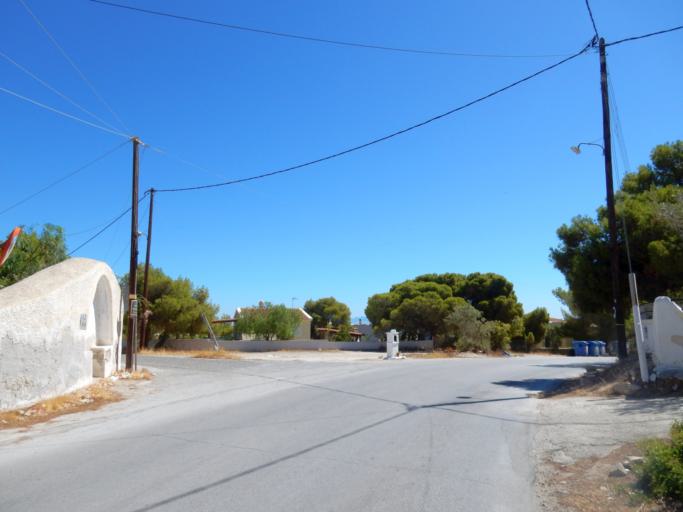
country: GR
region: Attica
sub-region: Nomos Piraios
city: Vathi
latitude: 37.7723
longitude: 23.5043
